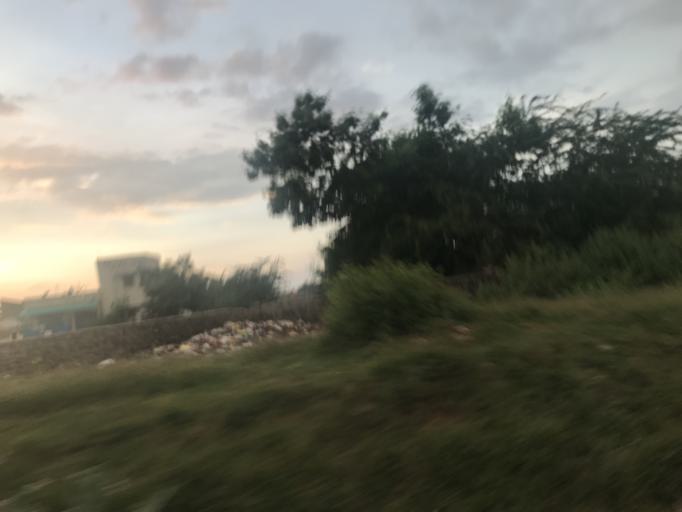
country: IN
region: Tamil Nadu
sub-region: Tiruppur
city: Tiruppur
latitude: 11.1231
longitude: 77.3673
